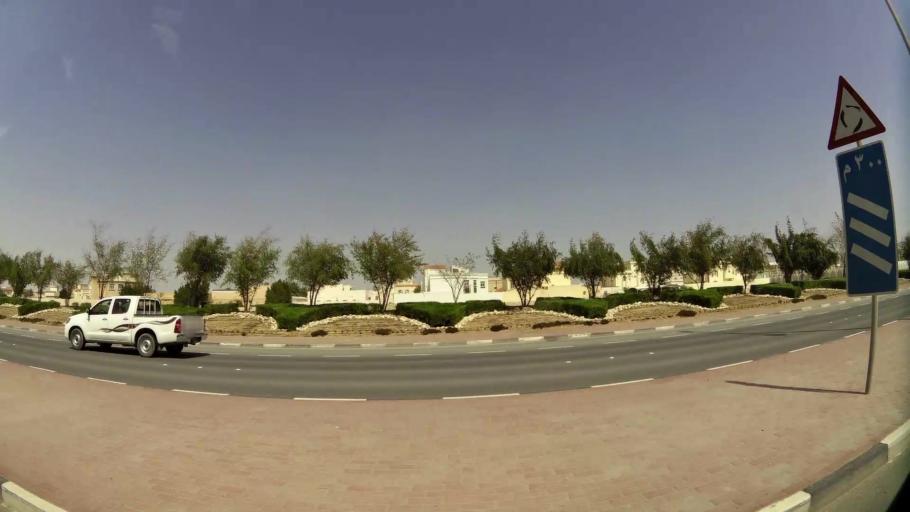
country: QA
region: Baladiyat Umm Salal
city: Umm Salal Muhammad
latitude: 25.3776
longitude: 51.4300
